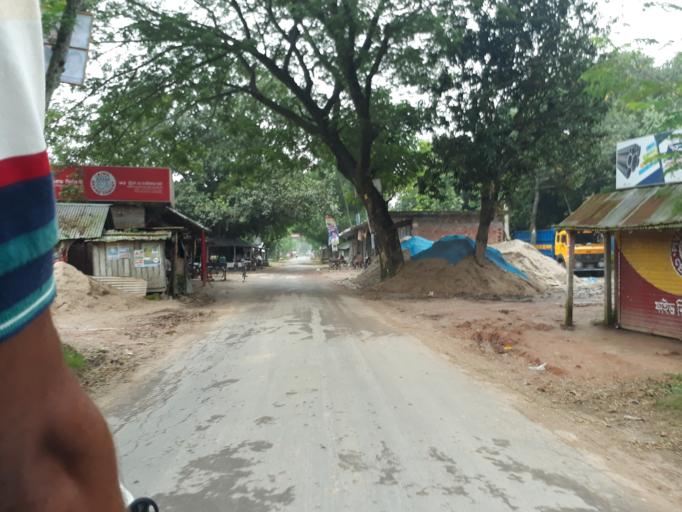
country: BD
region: Khulna
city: Kaliganj
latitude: 23.3511
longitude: 88.9238
